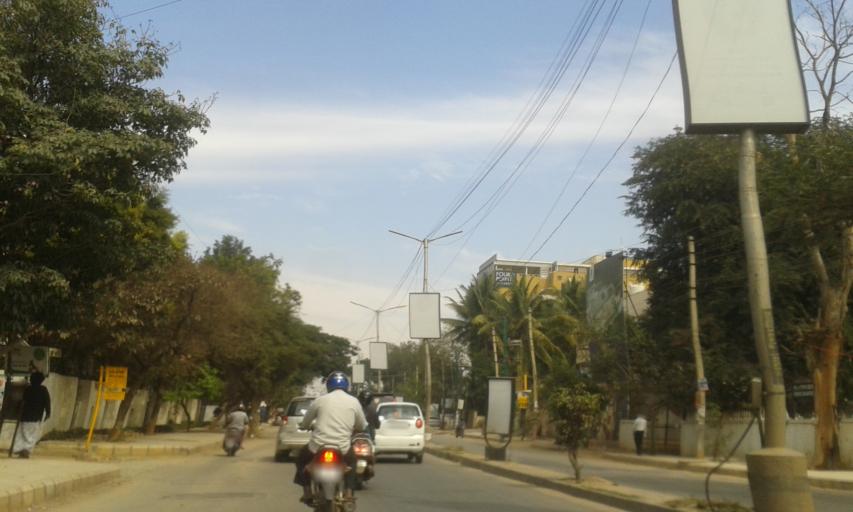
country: IN
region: Karnataka
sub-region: Bangalore Rural
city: Hoskote
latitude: 12.9780
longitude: 77.7512
